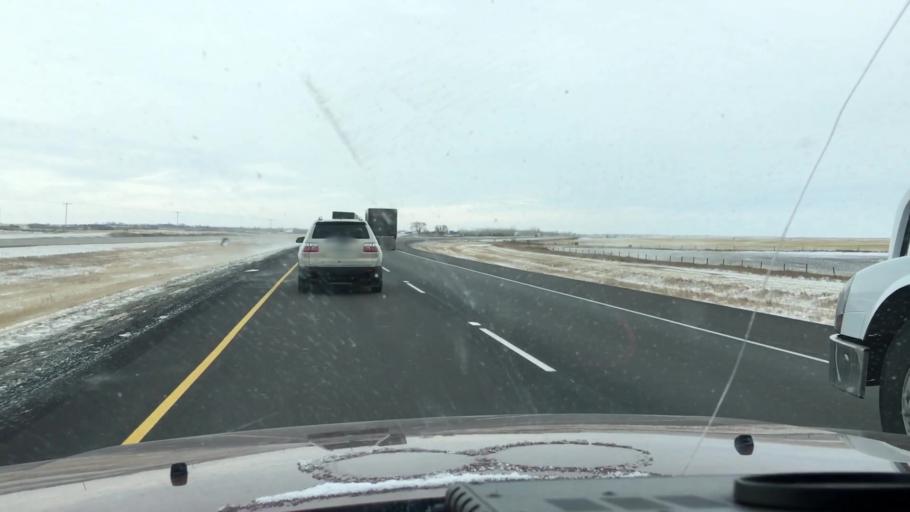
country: CA
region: Saskatchewan
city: Saskatoon
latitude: 51.7816
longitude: -106.4778
